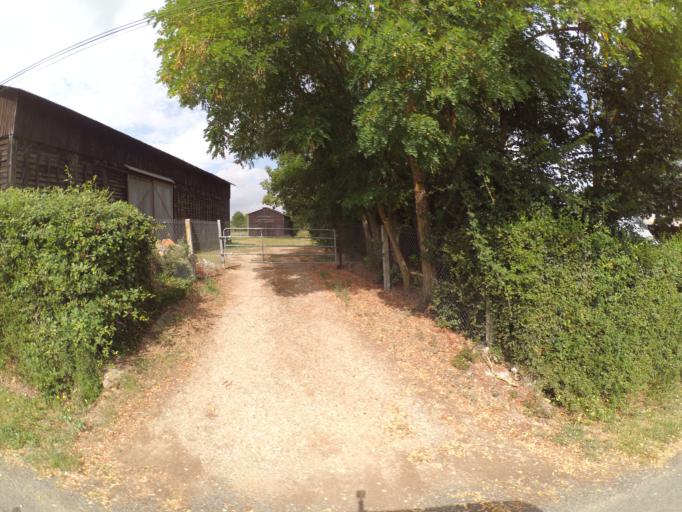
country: FR
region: Pays de la Loire
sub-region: Departement de Maine-et-Loire
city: Saint-Jean
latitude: 47.1945
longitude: -0.3682
